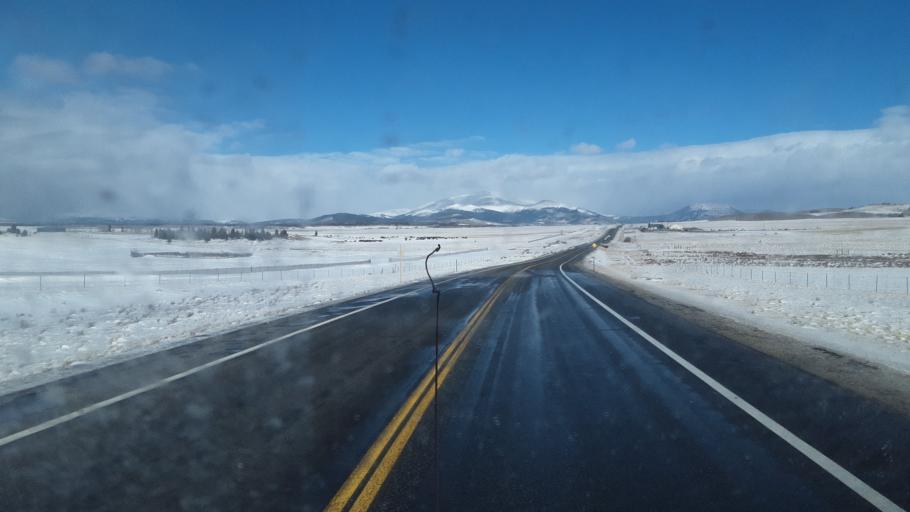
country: US
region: Colorado
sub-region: Park County
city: Fairplay
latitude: 39.1696
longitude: -106.0015
